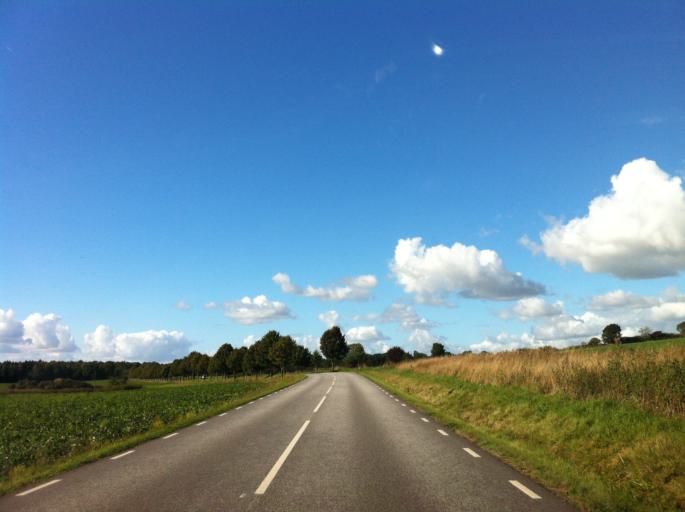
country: SE
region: Skane
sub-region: Sjobo Kommun
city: Sjoebo
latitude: 55.6779
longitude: 13.6548
